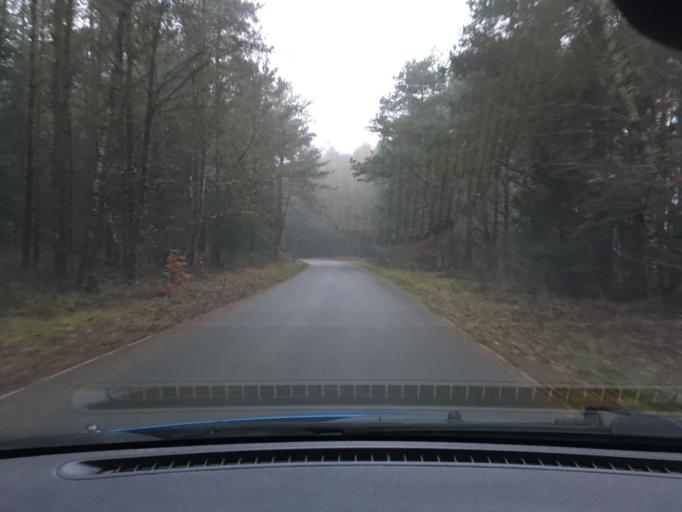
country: DE
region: Lower Saxony
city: Oldendorf
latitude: 53.1524
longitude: 10.1858
